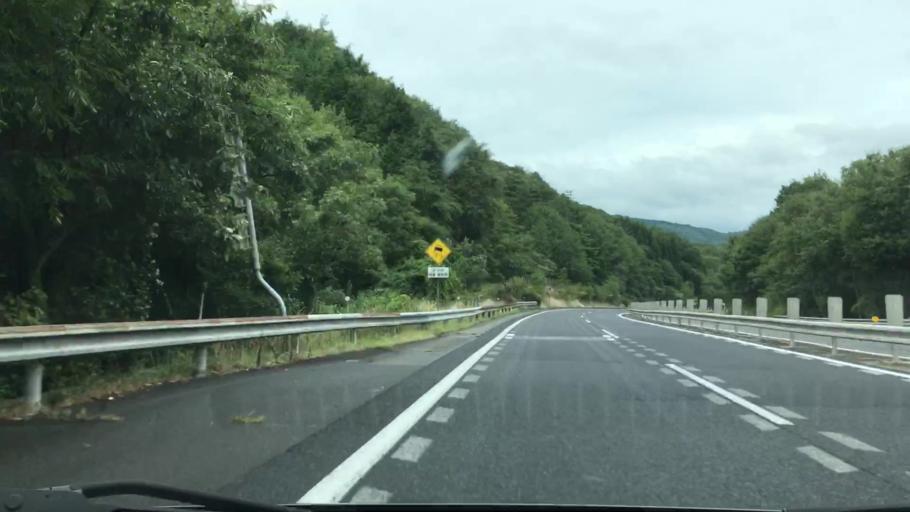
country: JP
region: Hyogo
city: Yamazakicho-nakabirose
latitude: 35.0073
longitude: 134.3335
